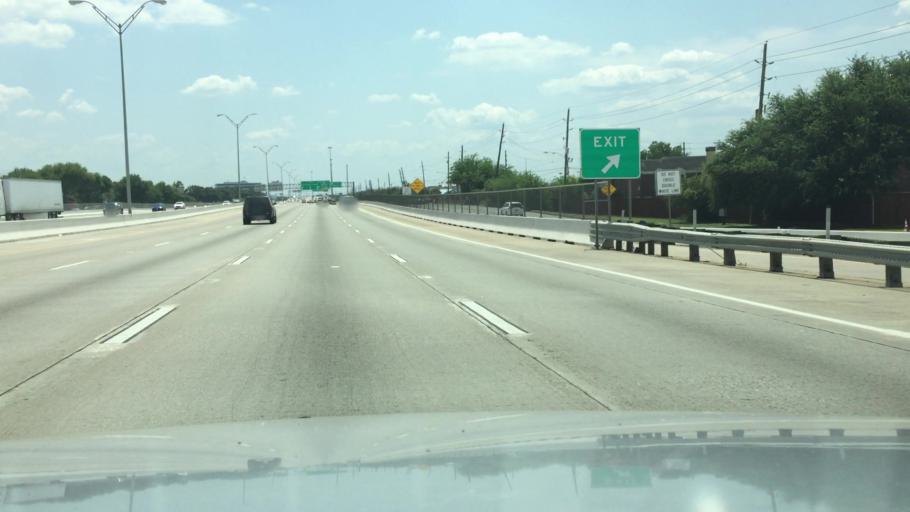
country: US
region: Texas
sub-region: Fort Bend County
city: Meadows Place
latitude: 29.6864
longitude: -95.5582
